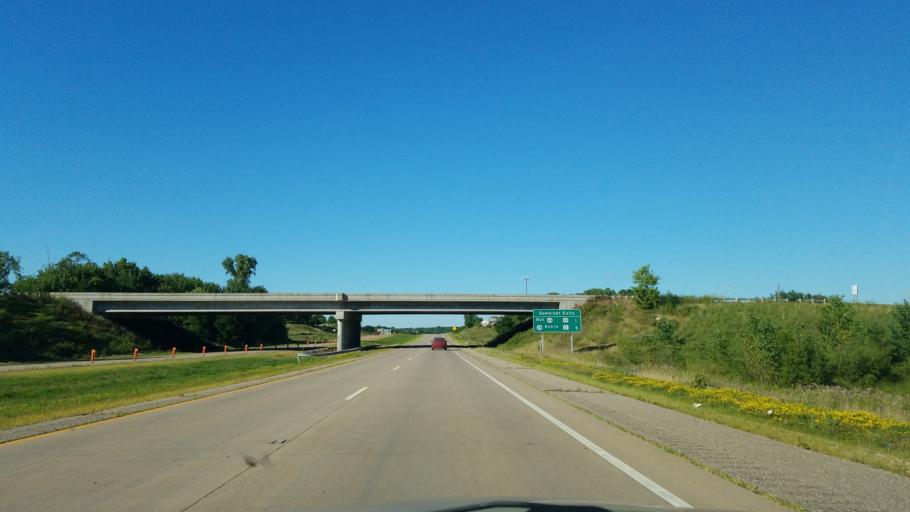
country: US
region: Minnesota
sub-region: Washington County
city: Stillwater
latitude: 45.0884
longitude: -92.7405
